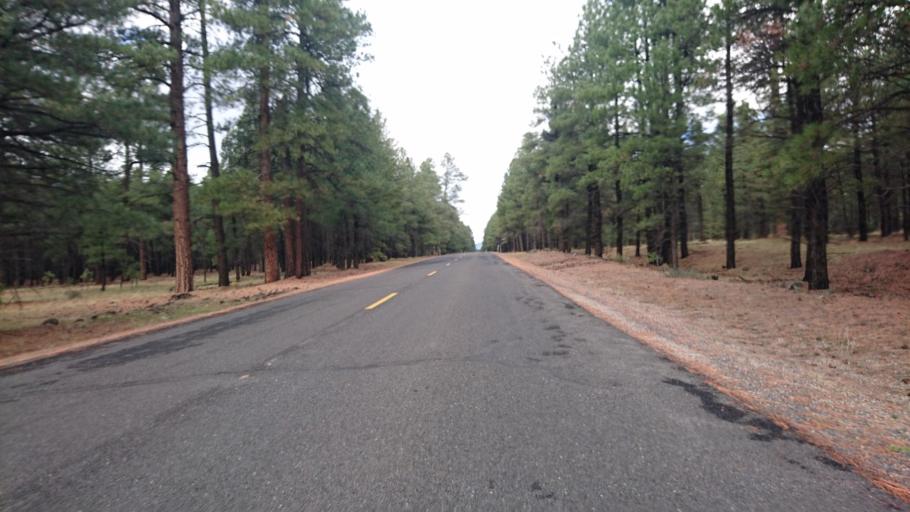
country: US
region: Arizona
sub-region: Coconino County
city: Parks
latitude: 35.2545
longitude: -111.8629
